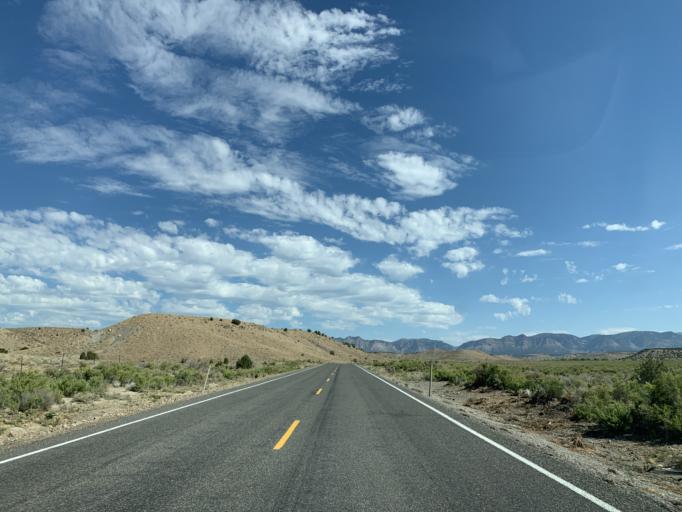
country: US
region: Utah
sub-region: Carbon County
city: Wellington
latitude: 39.5716
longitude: -110.6536
